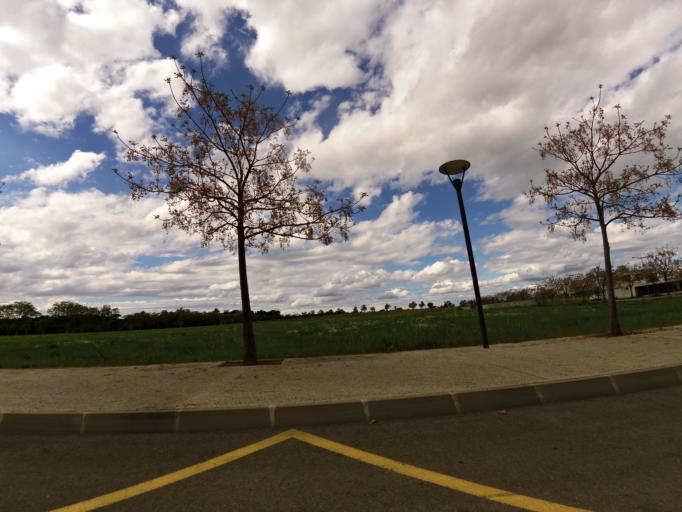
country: FR
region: Languedoc-Roussillon
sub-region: Departement de l'Herault
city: Lunel
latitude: 43.6896
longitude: 4.1352
